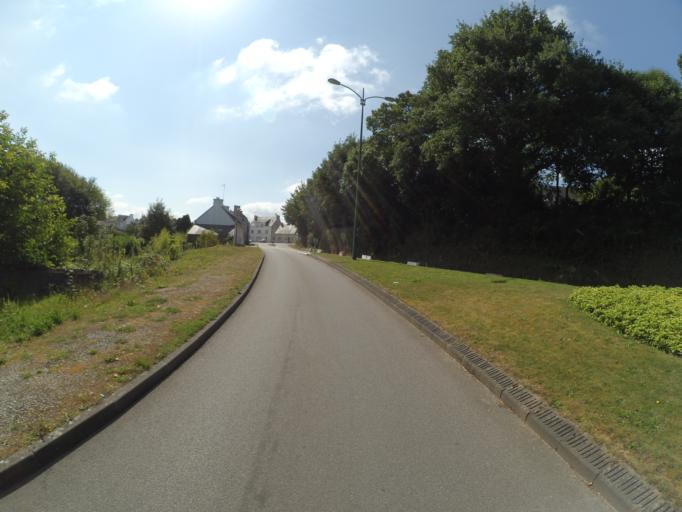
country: FR
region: Brittany
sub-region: Departement du Finistere
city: Bannalec
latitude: 47.9330
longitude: -3.7030
